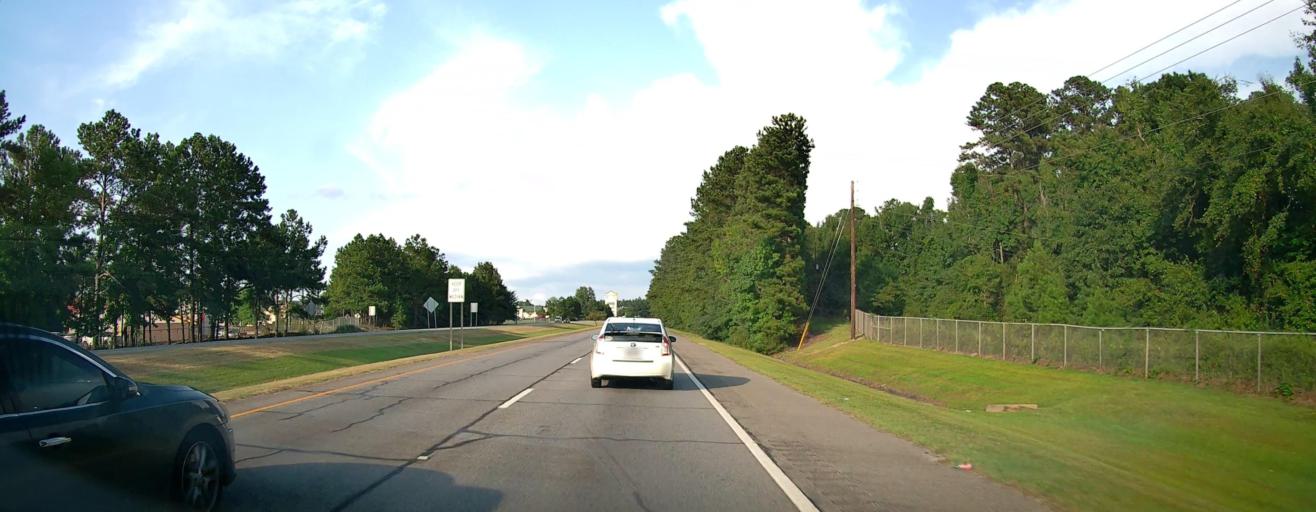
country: US
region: Georgia
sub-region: Bibb County
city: Macon
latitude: 32.8130
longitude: -83.7186
